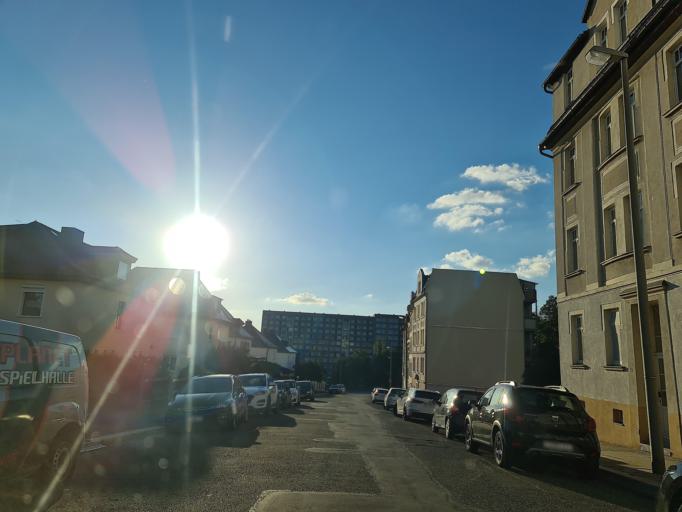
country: DE
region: Thuringia
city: Gera
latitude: 50.8936
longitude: 12.0860
